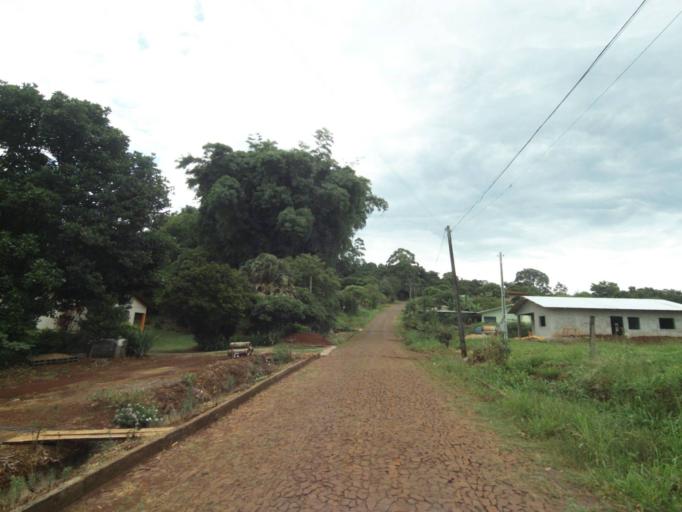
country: BR
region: Parana
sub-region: Guaraniacu
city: Guaraniacu
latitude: -25.0938
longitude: -52.8655
